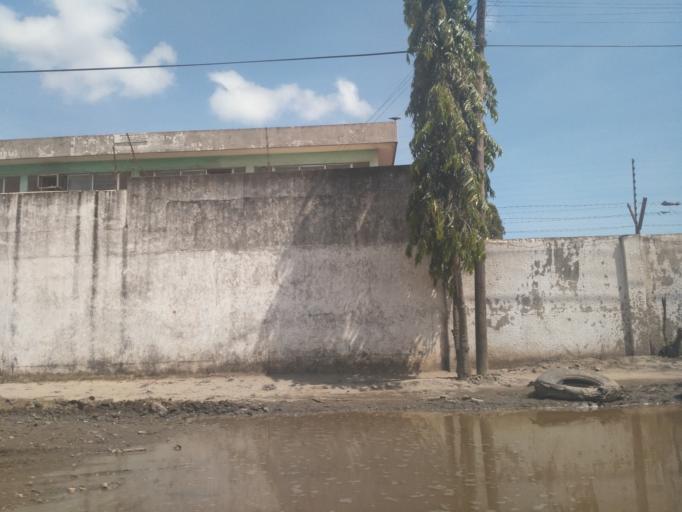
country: TZ
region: Dar es Salaam
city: Dar es Salaam
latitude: -6.8410
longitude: 39.2675
